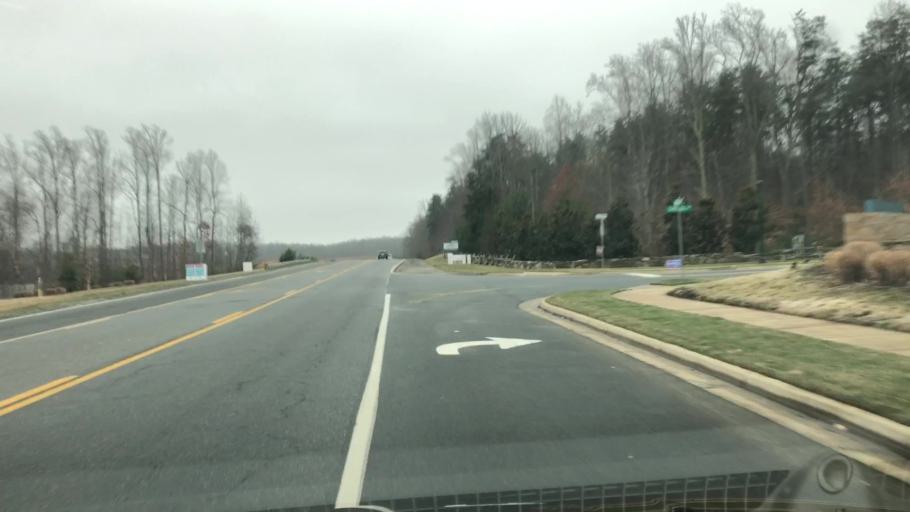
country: US
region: Virginia
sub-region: Stafford County
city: Stafford
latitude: 38.4302
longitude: -77.4259
